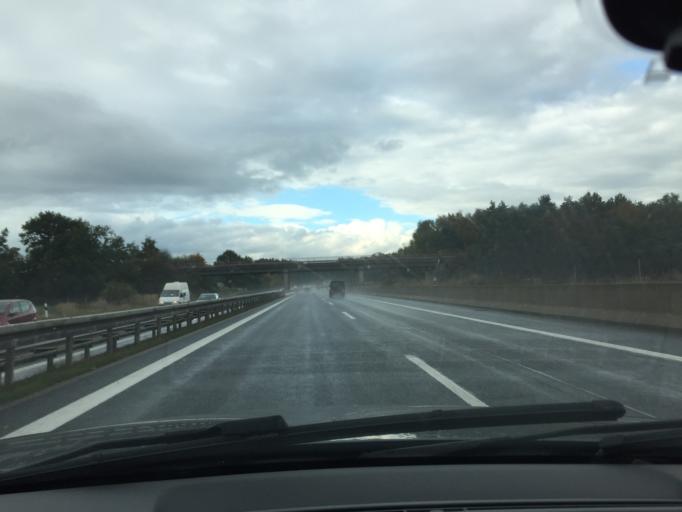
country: DE
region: Saxony
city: Radeburg
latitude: 51.2263
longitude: 13.7298
